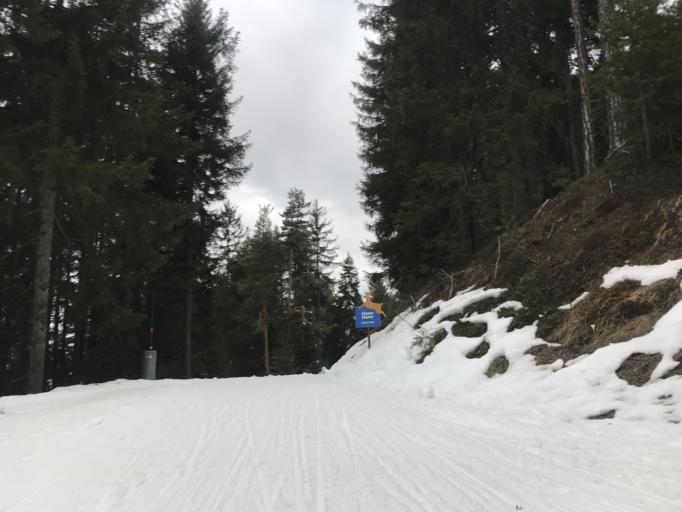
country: IT
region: Trentino-Alto Adige
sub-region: Bolzano
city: Bressanone
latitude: 46.6860
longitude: 11.6843
